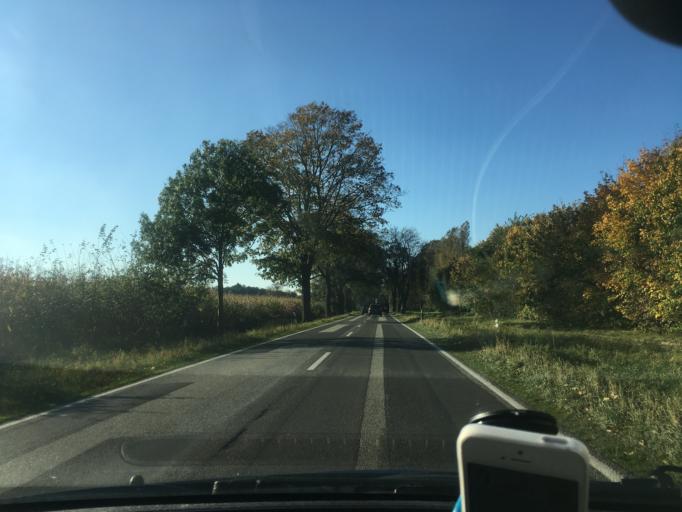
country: DE
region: Mecklenburg-Vorpommern
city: Zarrentin
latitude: 53.5315
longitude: 10.9538
